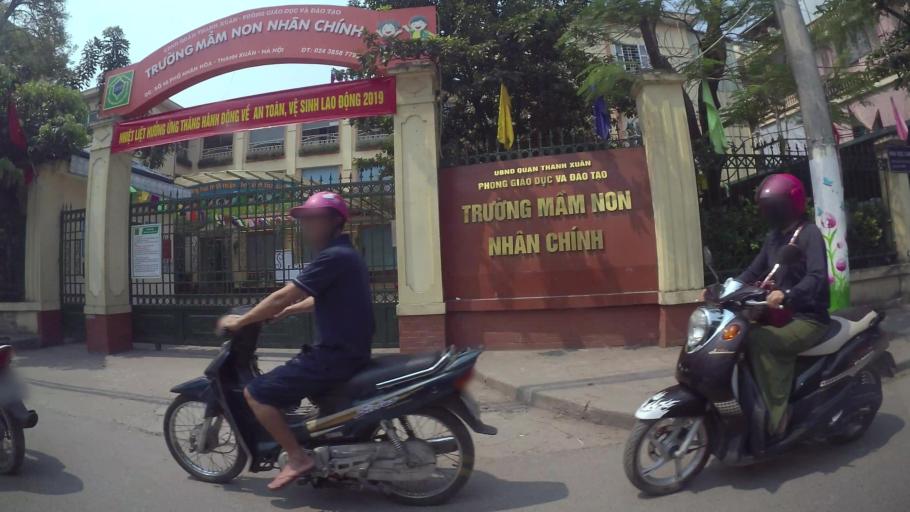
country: VN
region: Ha Noi
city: Thanh Xuan
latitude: 21.0021
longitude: 105.8090
